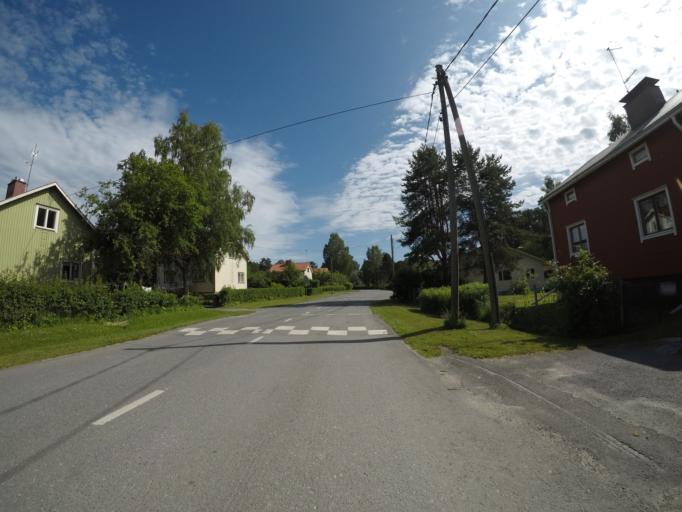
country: FI
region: Haeme
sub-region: Haemeenlinna
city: Haemeenlinna
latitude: 60.9883
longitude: 24.4057
